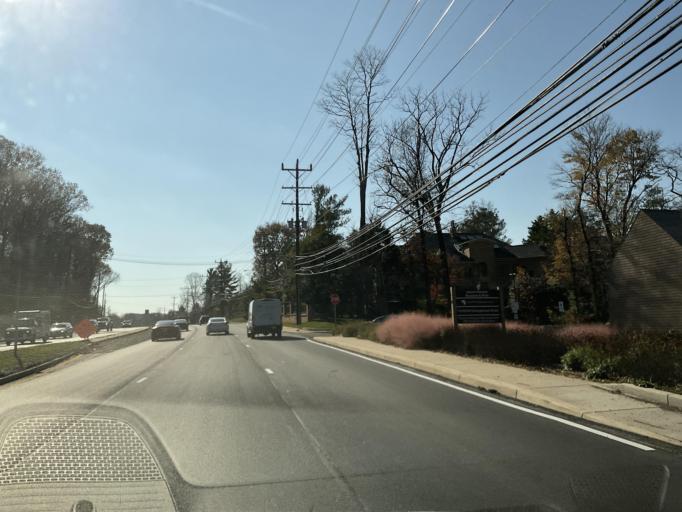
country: US
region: Maryland
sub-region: Montgomery County
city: North Bethesda
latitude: 39.0437
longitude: -77.1212
